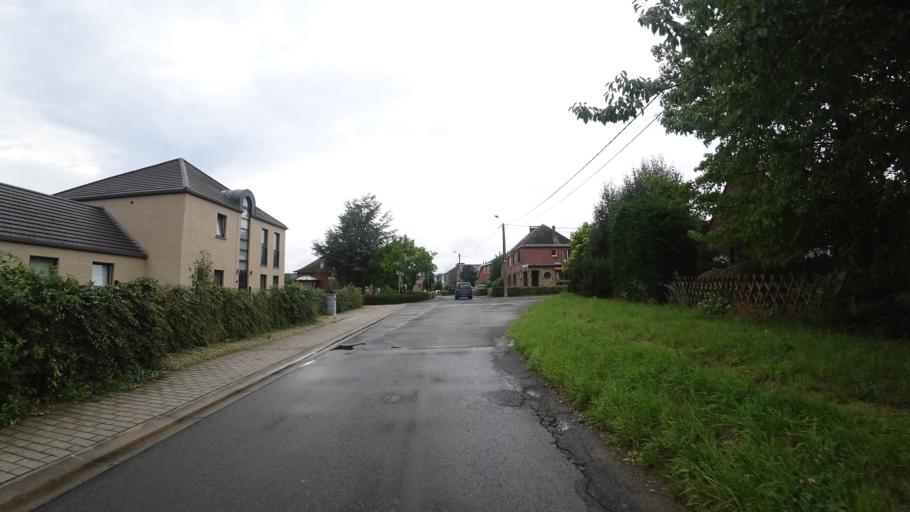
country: BE
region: Wallonia
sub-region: Province de Namur
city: Namur
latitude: 50.4595
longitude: 4.8234
